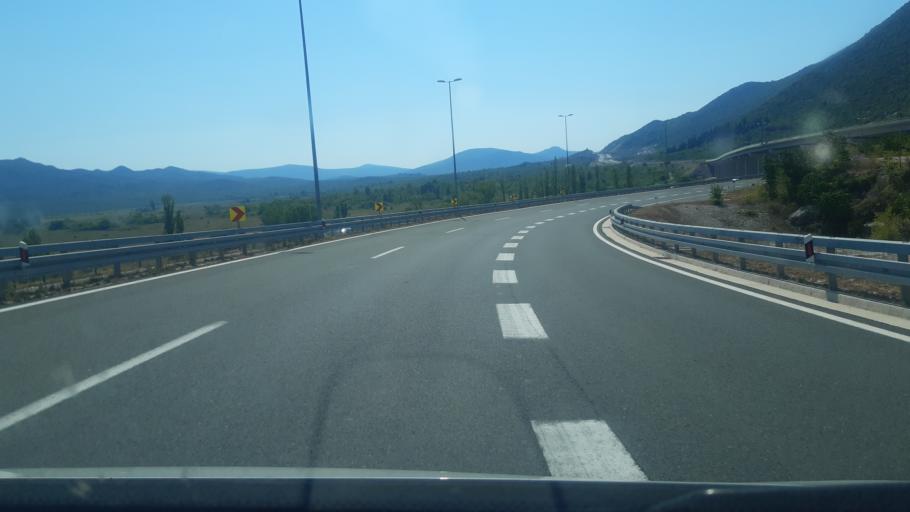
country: BA
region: Federation of Bosnia and Herzegovina
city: Ljubuski
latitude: 43.1479
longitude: 17.4886
